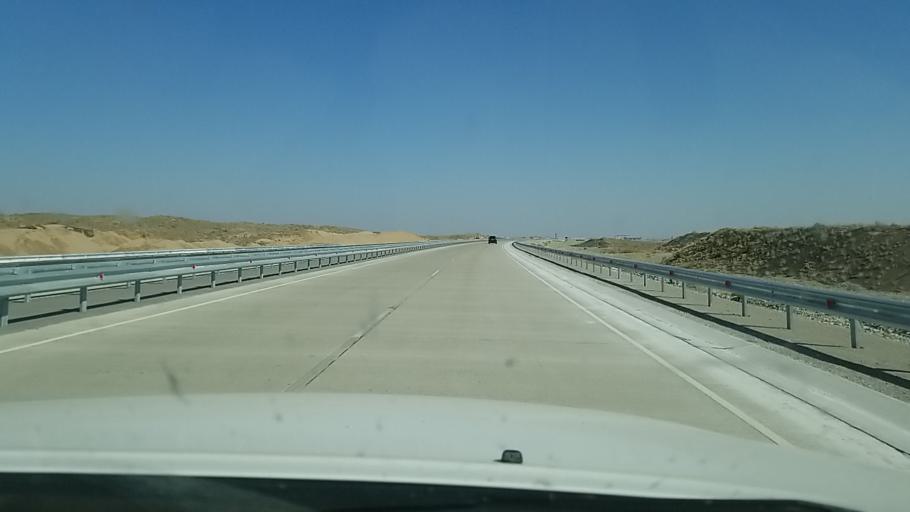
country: KZ
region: Almaty Oblysy
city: Zharkent
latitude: 44.1740
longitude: 80.3336
